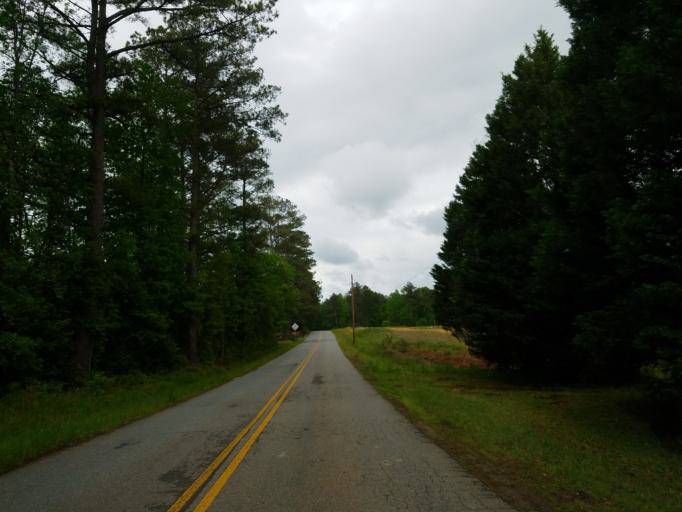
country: US
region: Georgia
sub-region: Lamar County
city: Barnesville
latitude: 33.1251
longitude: -84.2186
